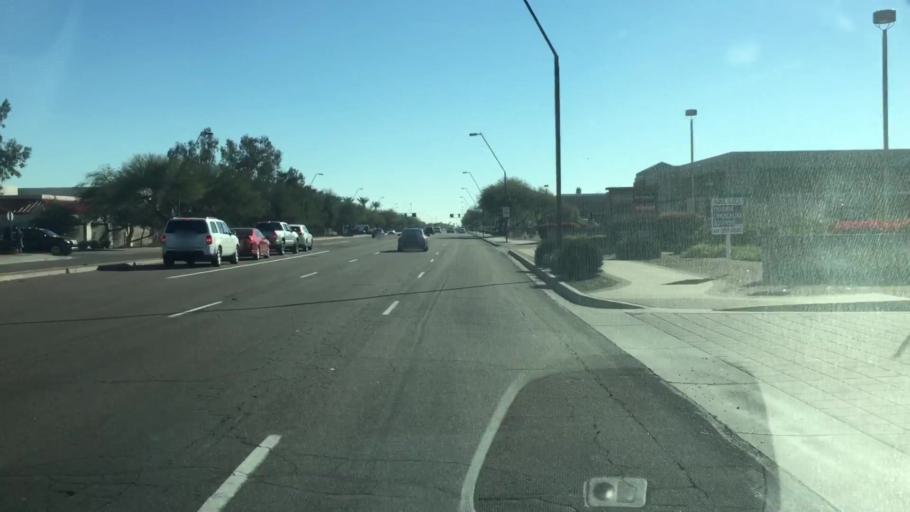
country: US
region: Arizona
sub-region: Maricopa County
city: Guadalupe
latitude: 33.3484
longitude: -111.9632
